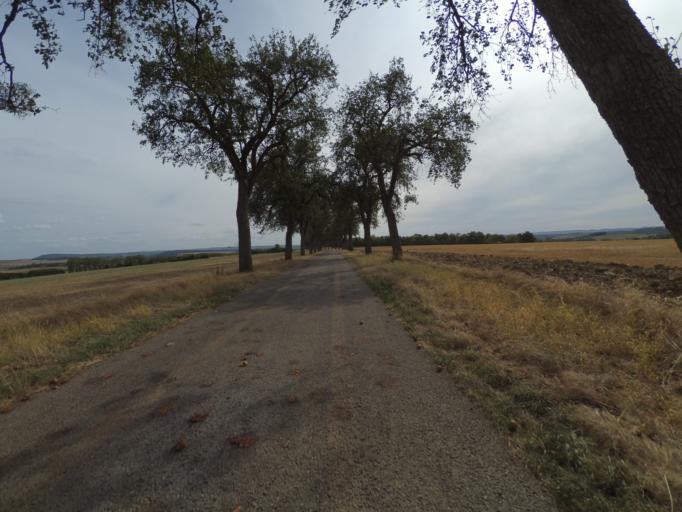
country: LU
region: Grevenmacher
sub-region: Canton de Remich
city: Mondorf-les-Bains
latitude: 49.5005
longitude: 6.2957
